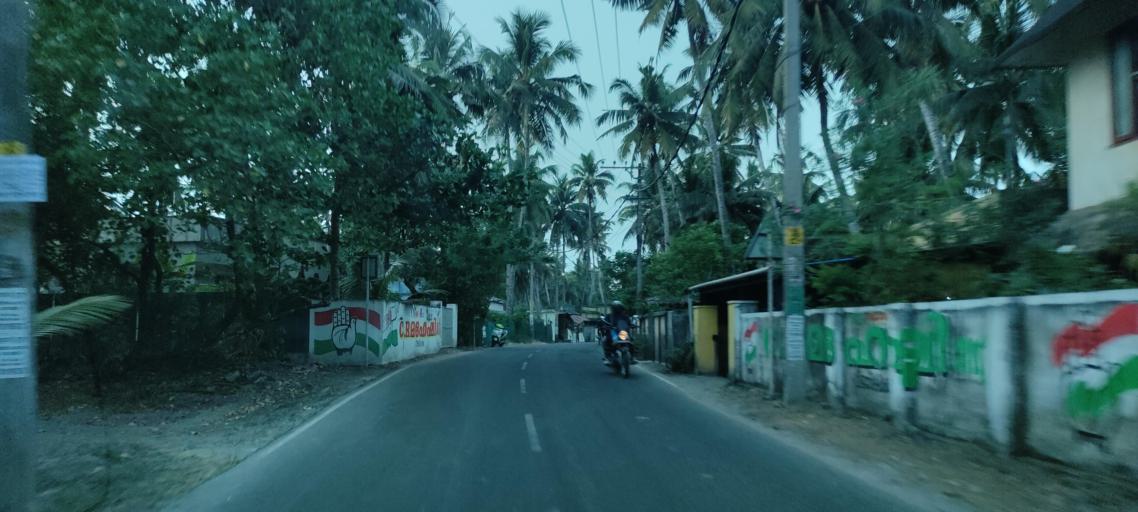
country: IN
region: Kerala
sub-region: Alappuzha
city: Kayankulam
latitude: 9.1155
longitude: 76.4729
